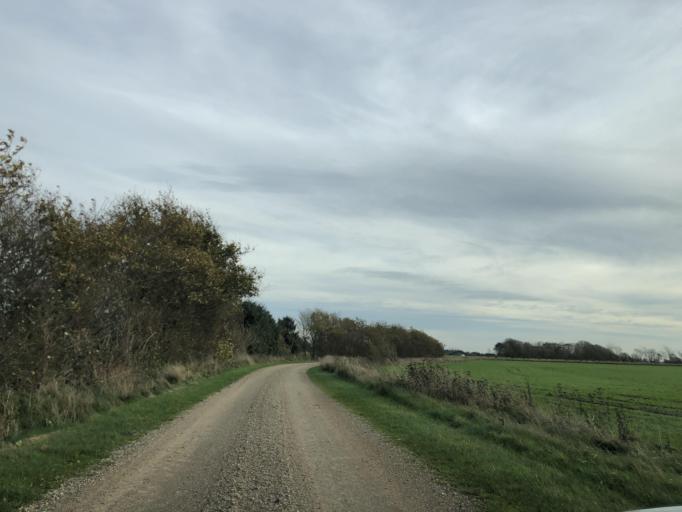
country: DK
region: South Denmark
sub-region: Tonder Kommune
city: Sherrebek
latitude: 55.1813
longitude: 8.7000
